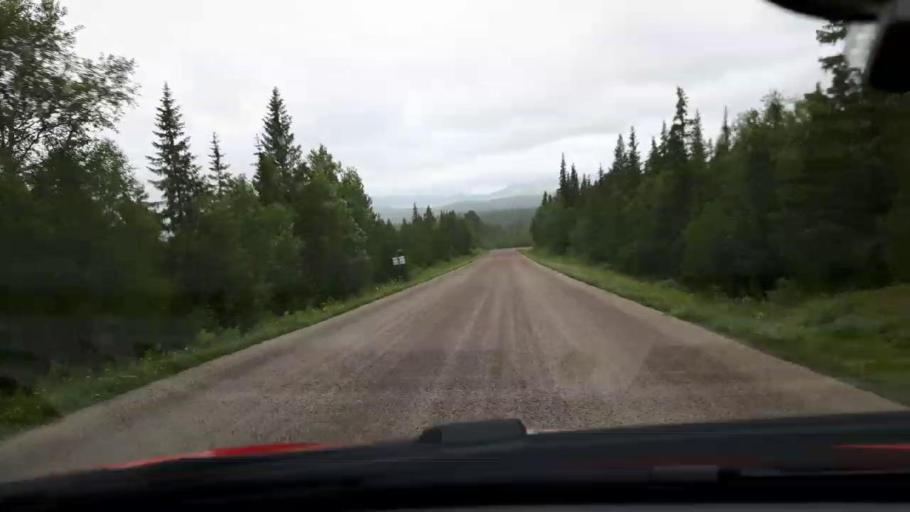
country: NO
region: Nord-Trondelag
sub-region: Meraker
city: Meraker
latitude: 63.2863
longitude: 12.3463
